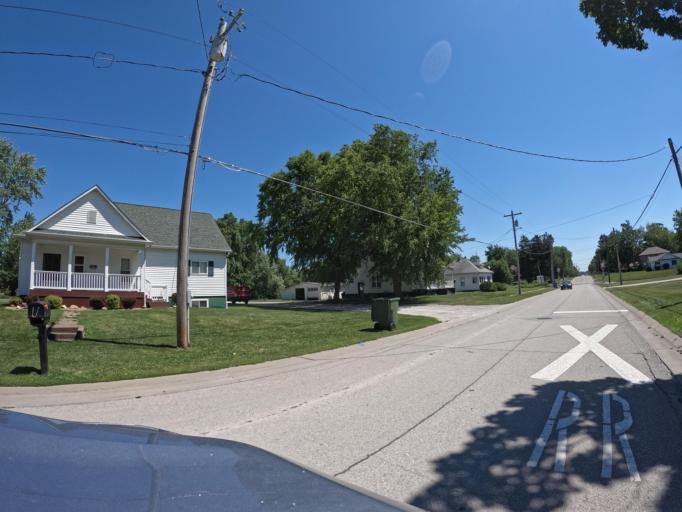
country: US
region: Iowa
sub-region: Monroe County
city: Albia
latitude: 41.0272
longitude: -92.7921
